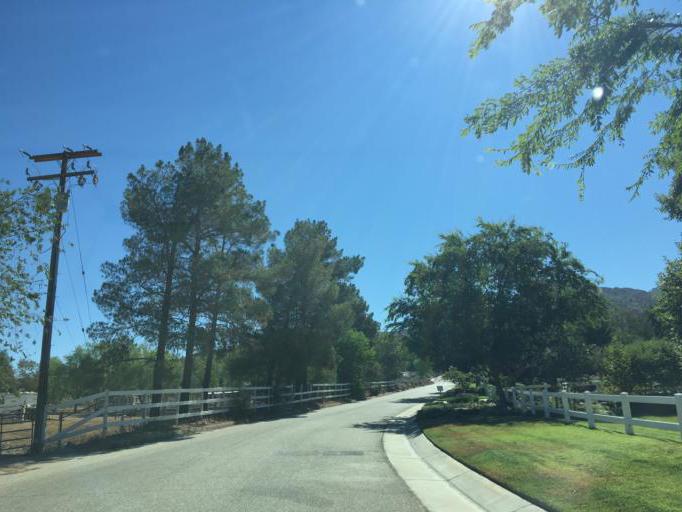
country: US
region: California
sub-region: Los Angeles County
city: Acton
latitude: 34.4713
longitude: -118.1607
